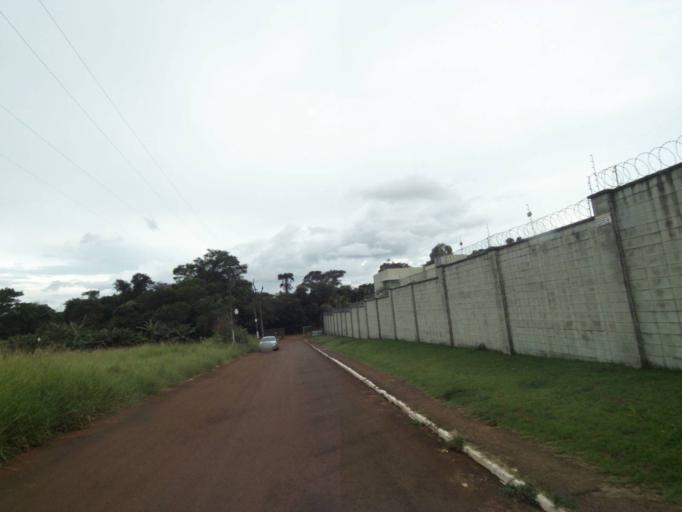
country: BR
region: Parana
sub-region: Campo Mourao
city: Campo Mourao
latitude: -24.0329
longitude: -52.3596
